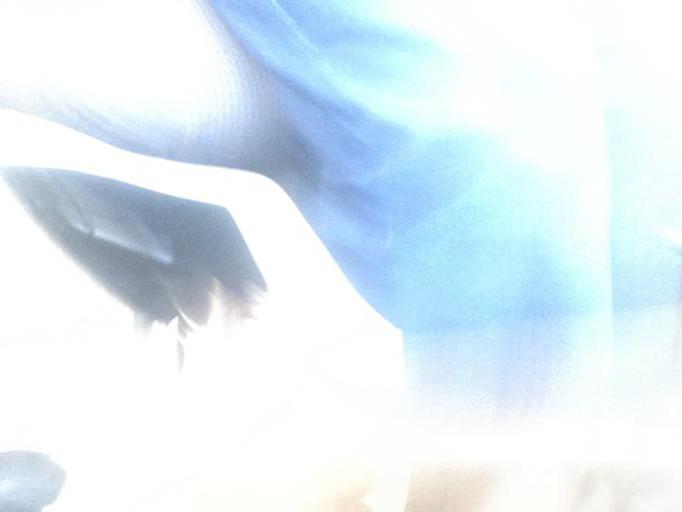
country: AU
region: New South Wales
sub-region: Blacktown
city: Blacktown
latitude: -33.7591
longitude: 150.8963
